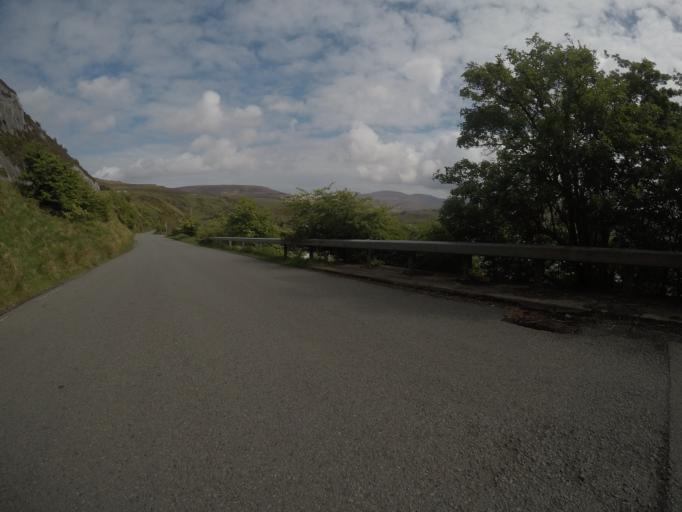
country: GB
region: Scotland
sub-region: Highland
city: Portree
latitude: 57.5905
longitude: -6.3793
